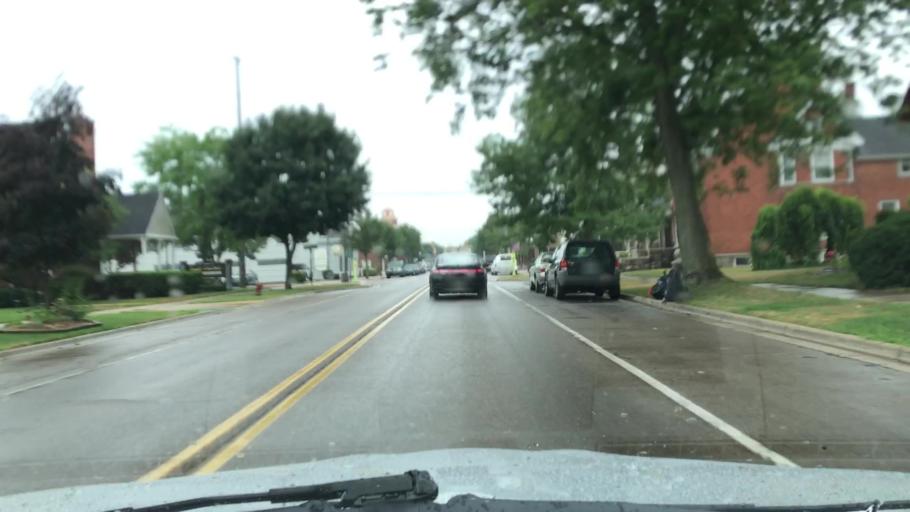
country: US
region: Michigan
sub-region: Macomb County
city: Utica
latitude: 42.6277
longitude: -83.0340
